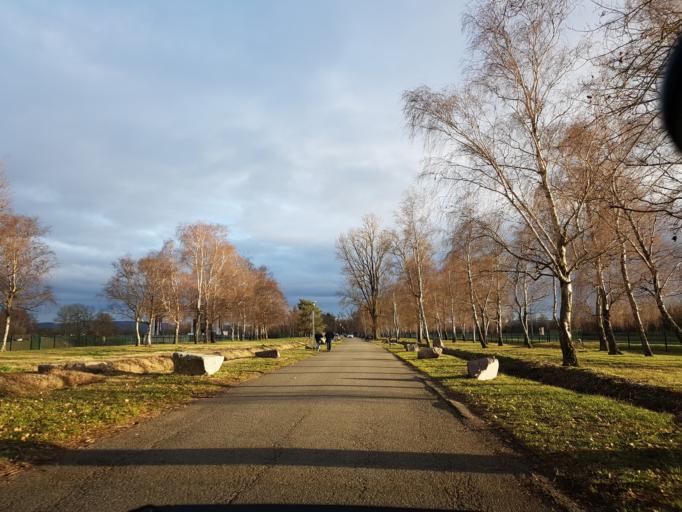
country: FR
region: Alsace
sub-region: Departement du Haut-Rhin
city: Rosenau
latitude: 47.6551
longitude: 7.5215
